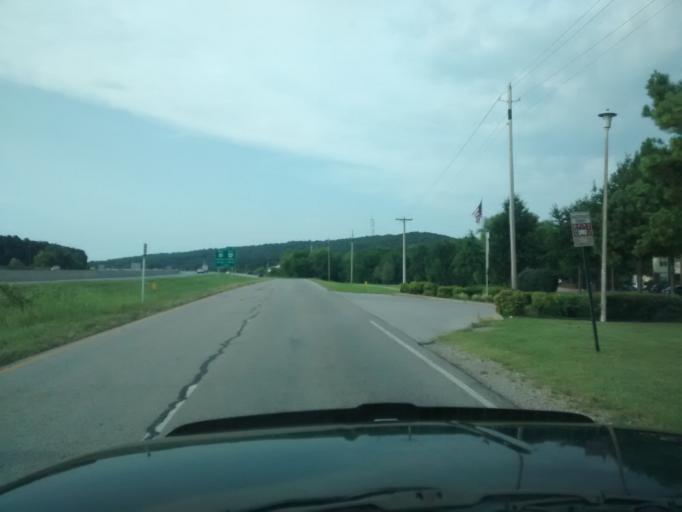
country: US
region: Arkansas
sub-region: Washington County
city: Fayetteville
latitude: 36.0748
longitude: -94.2029
